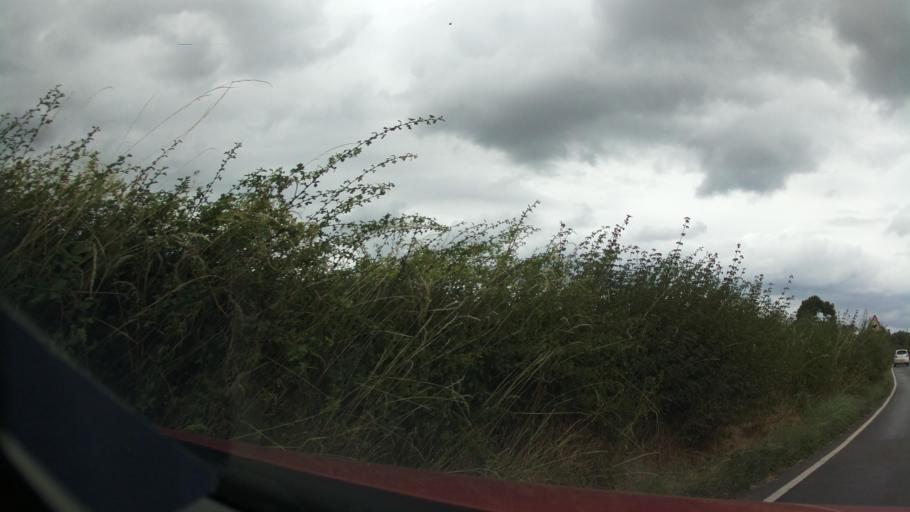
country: GB
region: England
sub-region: Derbyshire
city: Long Eaton
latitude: 52.9076
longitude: -1.3191
